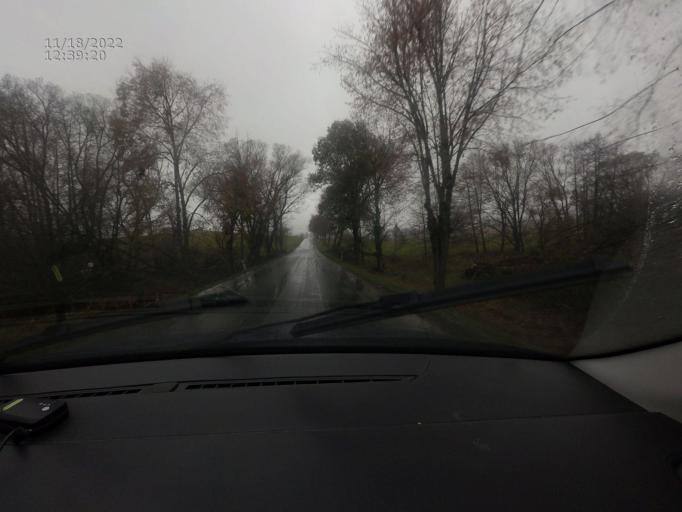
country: CZ
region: Plzensky
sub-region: Okres Klatovy
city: Planice
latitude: 49.3854
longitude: 13.4917
